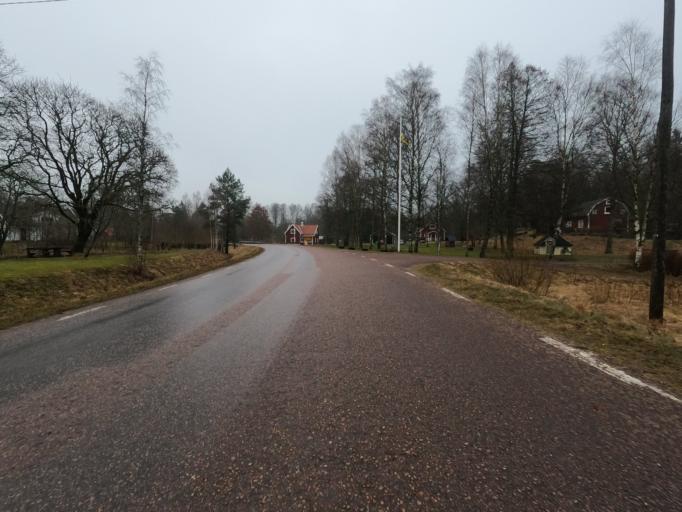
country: SE
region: Halland
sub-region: Hylte Kommun
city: Hyltebruk
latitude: 56.8091
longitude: 13.2698
